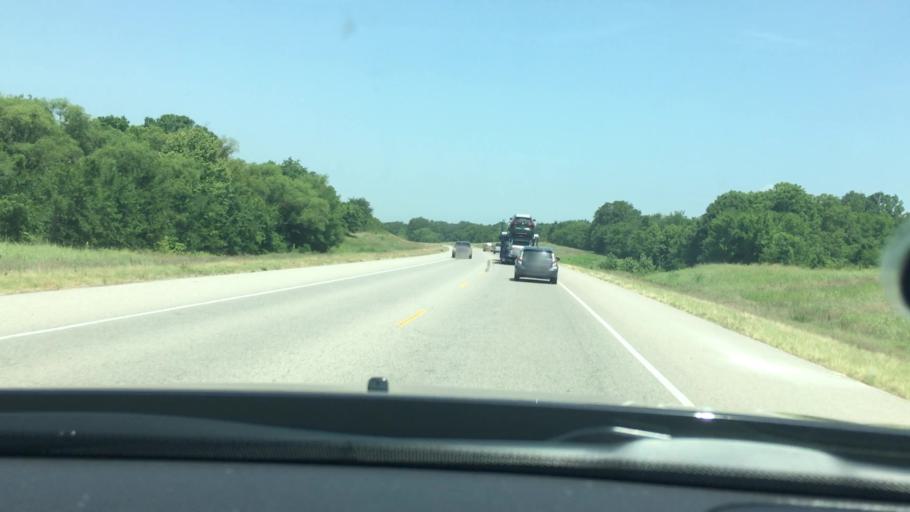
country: US
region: Oklahoma
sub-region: Pontotoc County
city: Ada
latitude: 34.6970
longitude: -96.5988
